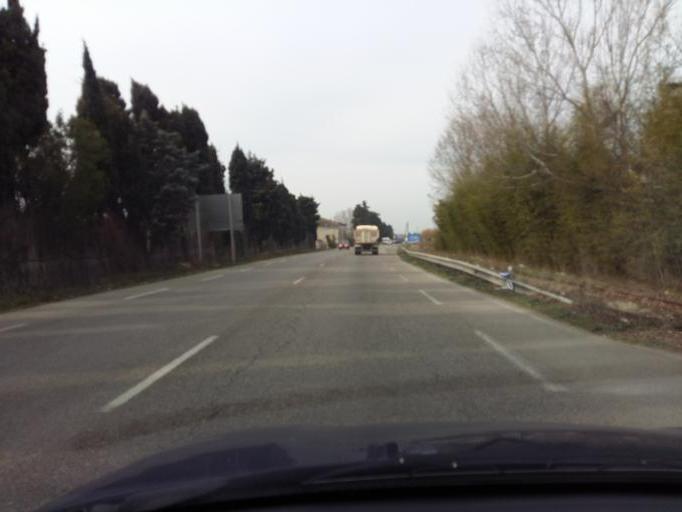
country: FR
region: Provence-Alpes-Cote d'Azur
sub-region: Departement des Bouches-du-Rhone
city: Chateaurenard
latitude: 43.8865
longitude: 4.8755
